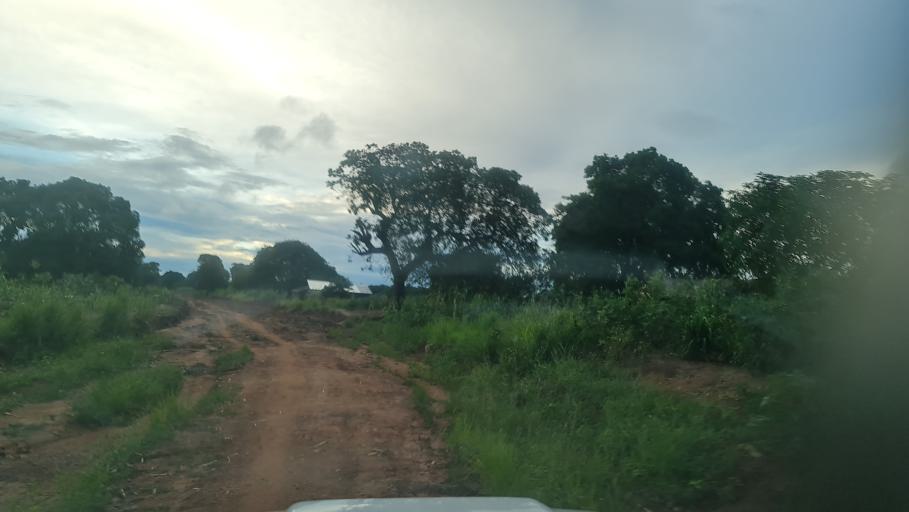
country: MZ
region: Nampula
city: Nacala
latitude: -14.7405
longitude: 39.9430
